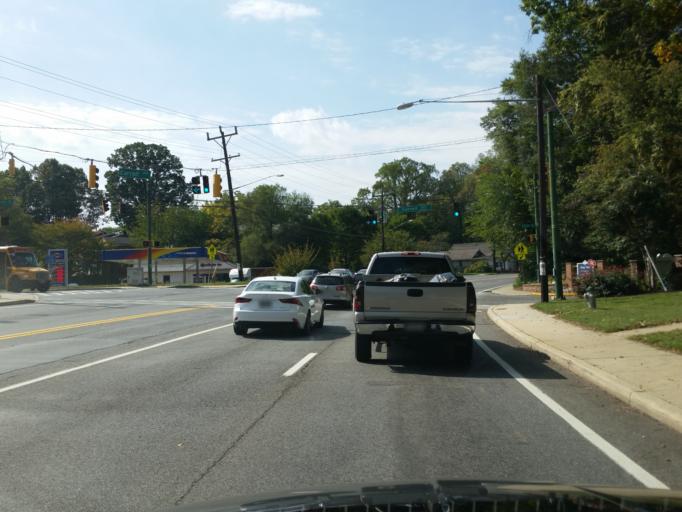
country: US
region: Maryland
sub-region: Prince George's County
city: Langley Park
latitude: 39.0002
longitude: -76.9903
